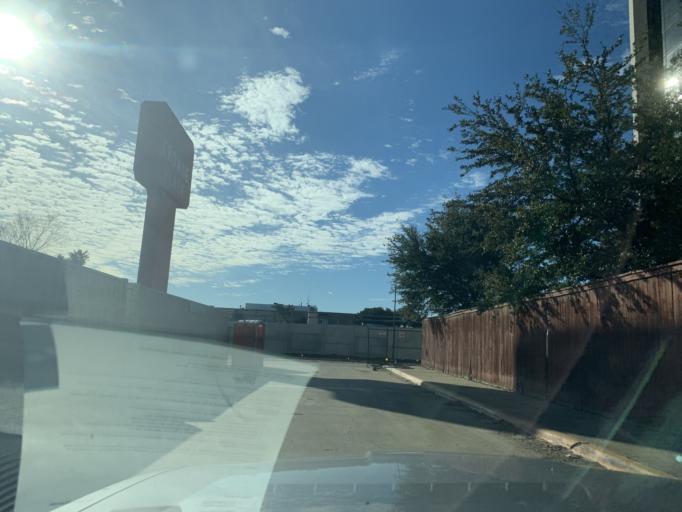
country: US
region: Texas
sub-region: Tarrant County
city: Arlington
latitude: 32.7606
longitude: -97.0560
